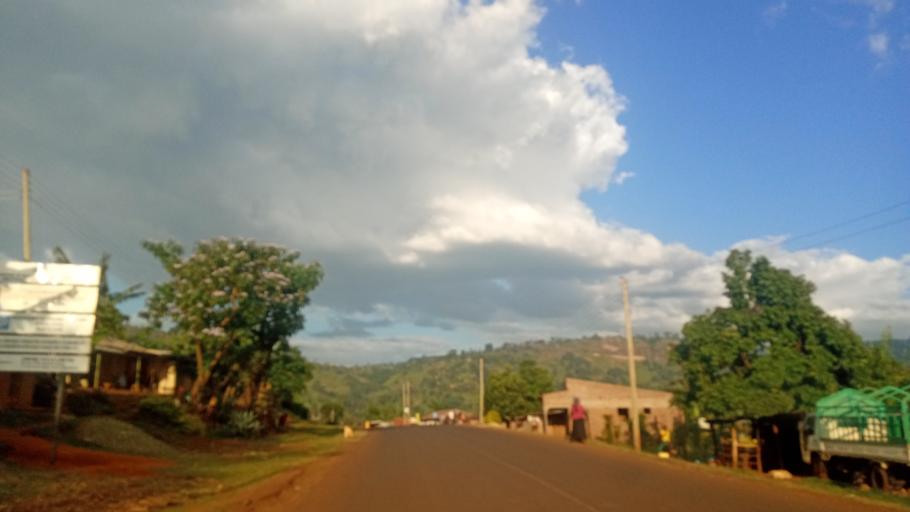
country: UG
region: Eastern Region
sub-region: Kapchorwa District
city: Kapchorwa
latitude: 1.3242
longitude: 34.3524
